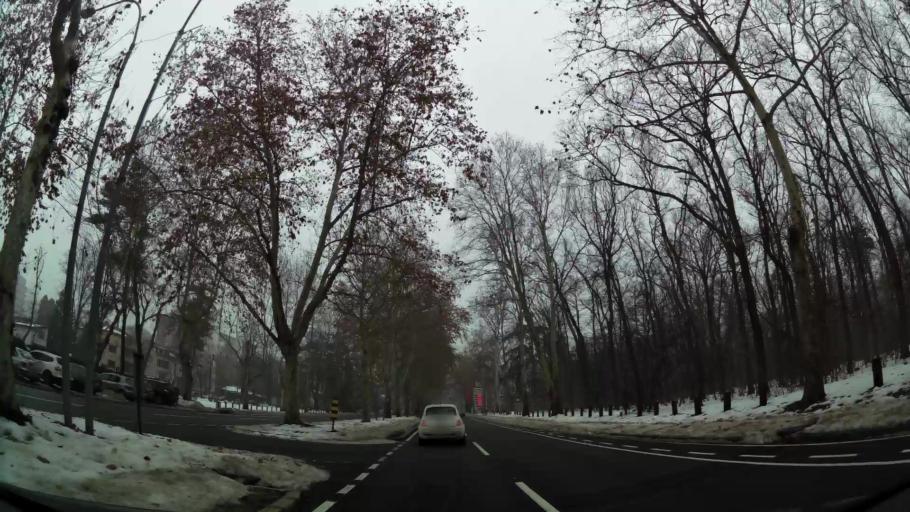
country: RS
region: Central Serbia
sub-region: Belgrade
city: Vozdovac
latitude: 44.7724
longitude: 20.4747
